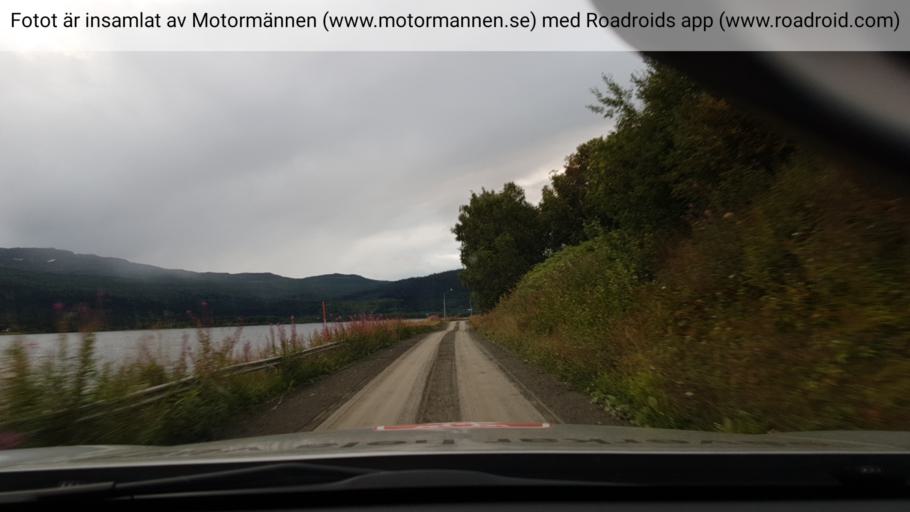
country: NO
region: Nordland
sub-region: Hattfjelldal
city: Hattfjelldal
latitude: 65.6506
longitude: 15.1750
